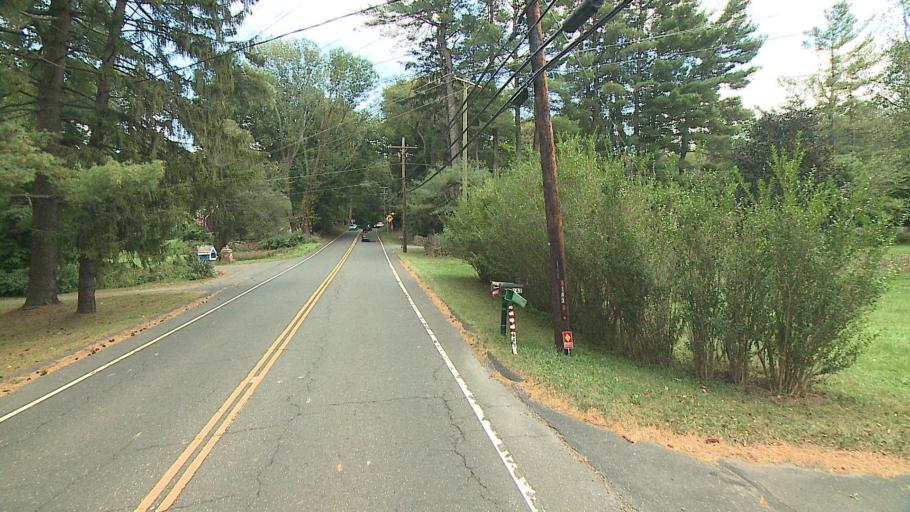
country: US
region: Connecticut
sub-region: Fairfield County
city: Wilton
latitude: 41.1786
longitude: -73.4031
